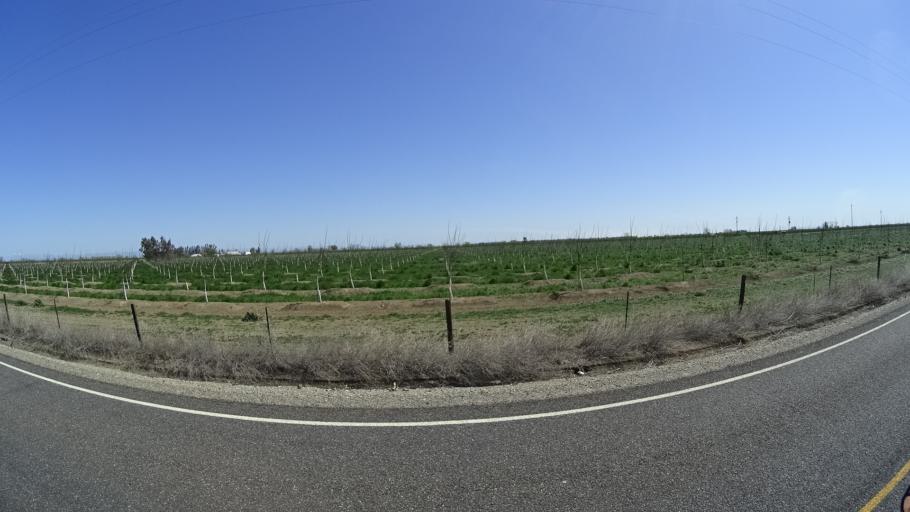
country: US
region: California
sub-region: Glenn County
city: Willows
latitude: 39.5990
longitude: -122.2500
